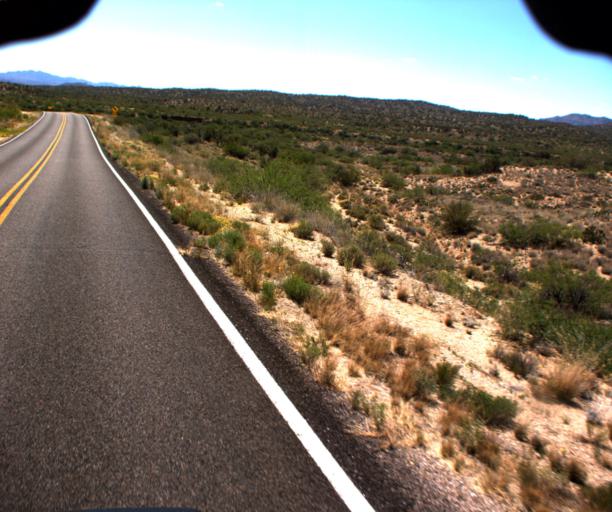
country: US
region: Arizona
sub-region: Yavapai County
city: Bagdad
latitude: 34.4999
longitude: -113.1710
